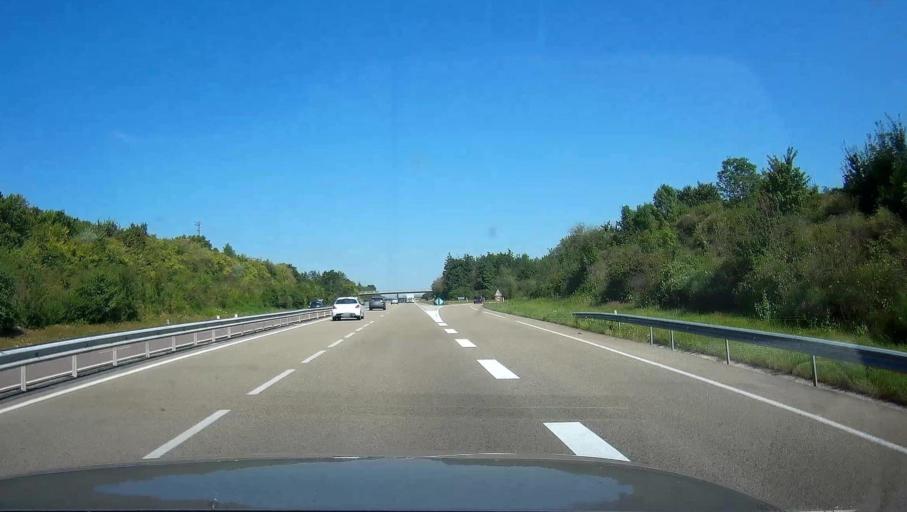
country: FR
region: Champagne-Ardenne
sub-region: Departement de l'Aube
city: Saint-Parres-aux-Tertres
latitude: 48.2885
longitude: 4.1652
